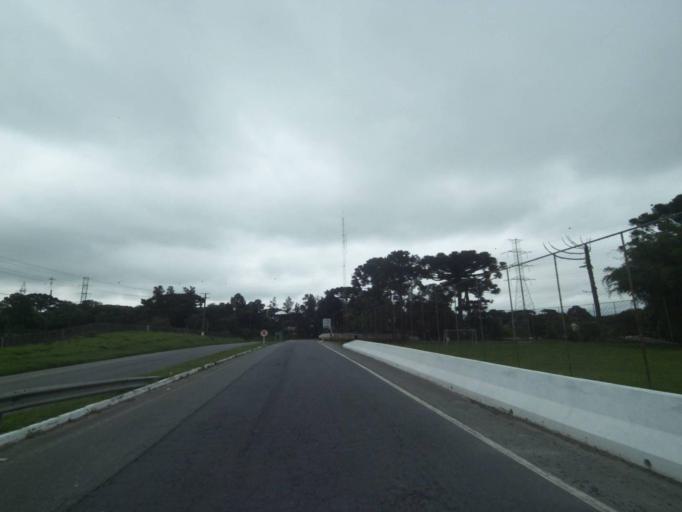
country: BR
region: Parana
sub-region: Curitiba
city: Curitiba
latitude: -25.4312
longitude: -49.3670
